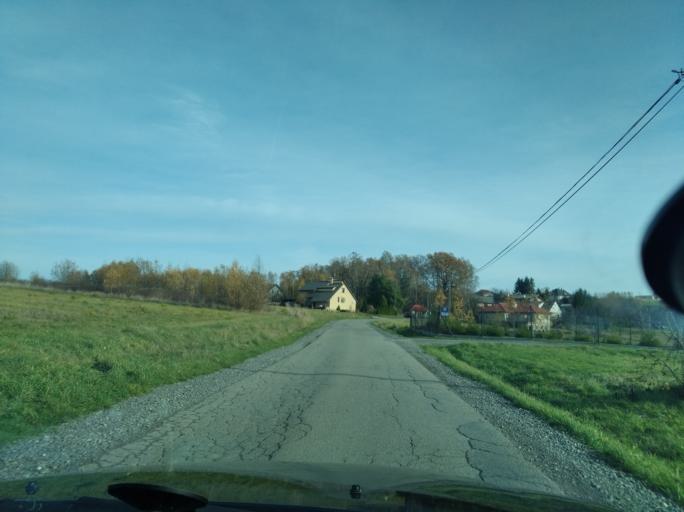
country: PL
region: Subcarpathian Voivodeship
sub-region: Powiat rzeszowski
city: Krasne
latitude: 50.0151
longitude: 22.0995
